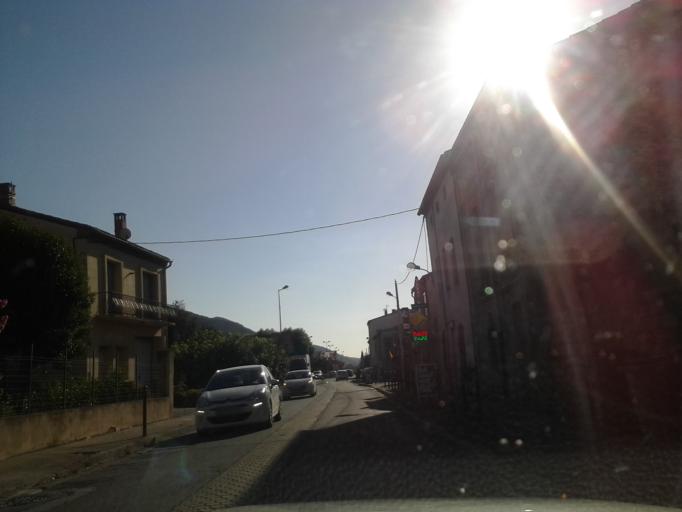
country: FR
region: Languedoc-Roussillon
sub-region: Departement des Pyrenees-Orientales
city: Vinca
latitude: 42.6419
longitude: 2.4835
